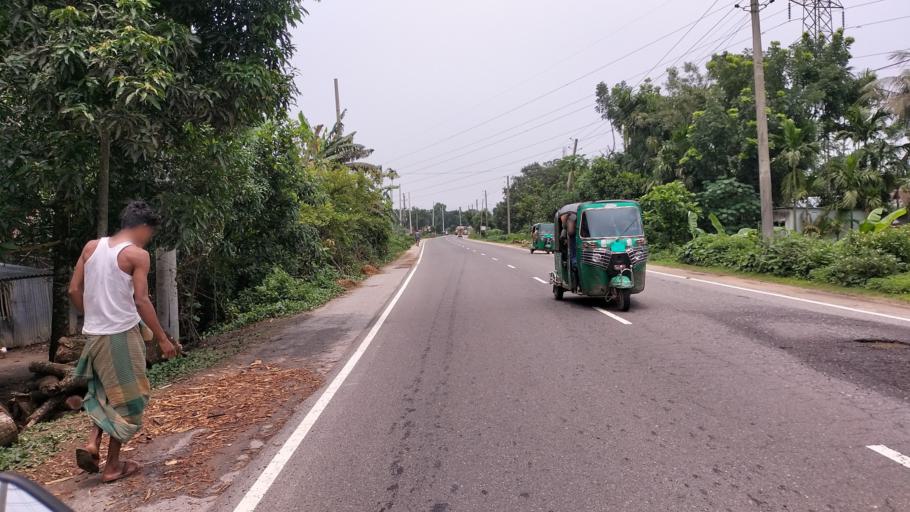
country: BD
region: Dhaka
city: Mymensingh
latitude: 24.7745
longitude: 90.4645
